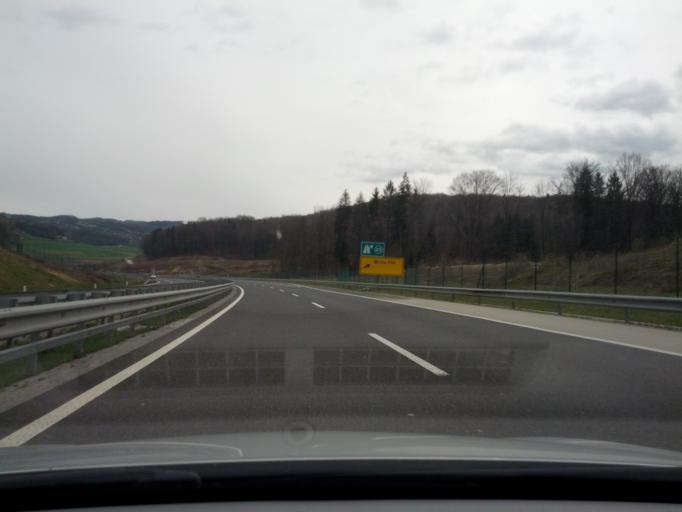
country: SI
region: Mirna Pec
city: Mirna Pec
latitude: 45.8735
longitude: 15.0934
